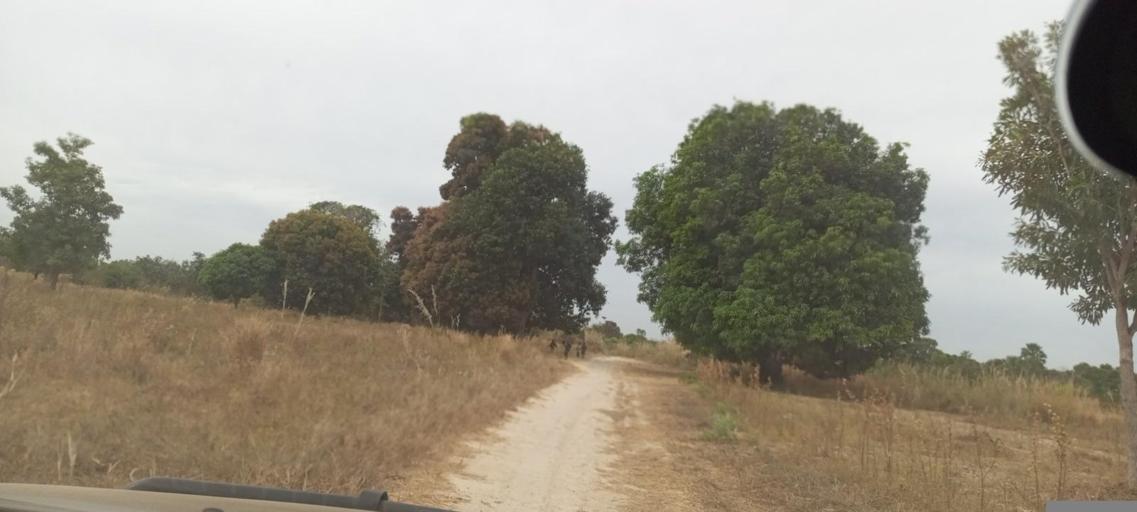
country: ML
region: Koulikoro
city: Kati
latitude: 12.7568
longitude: -8.3058
